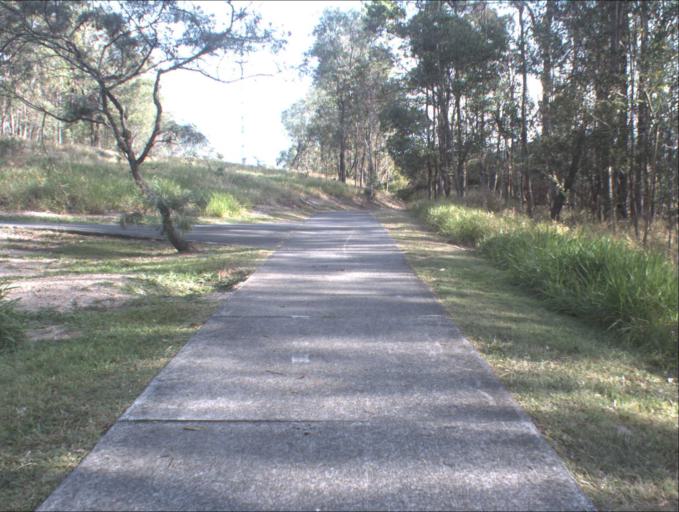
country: AU
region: Queensland
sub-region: Logan
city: Slacks Creek
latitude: -27.6310
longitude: 153.1475
